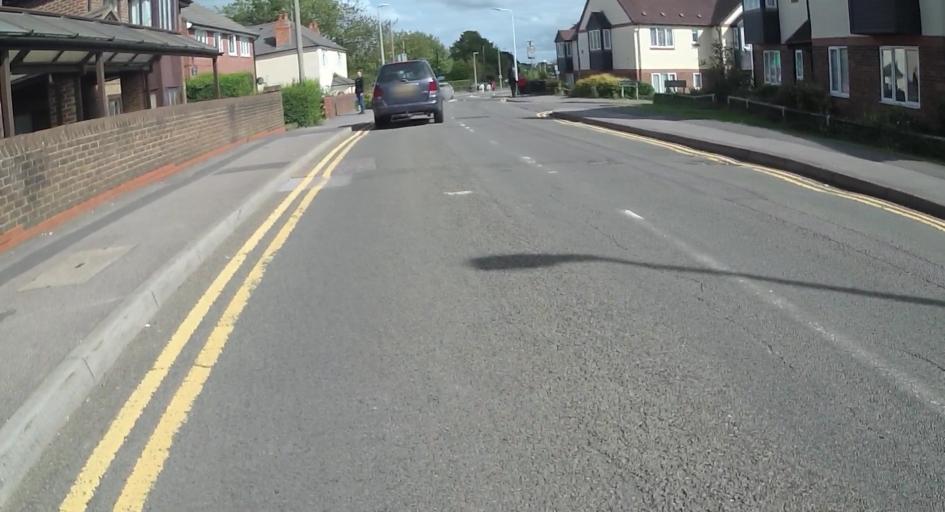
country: GB
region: England
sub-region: West Berkshire
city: Thatcham
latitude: 51.4017
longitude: -1.2554
